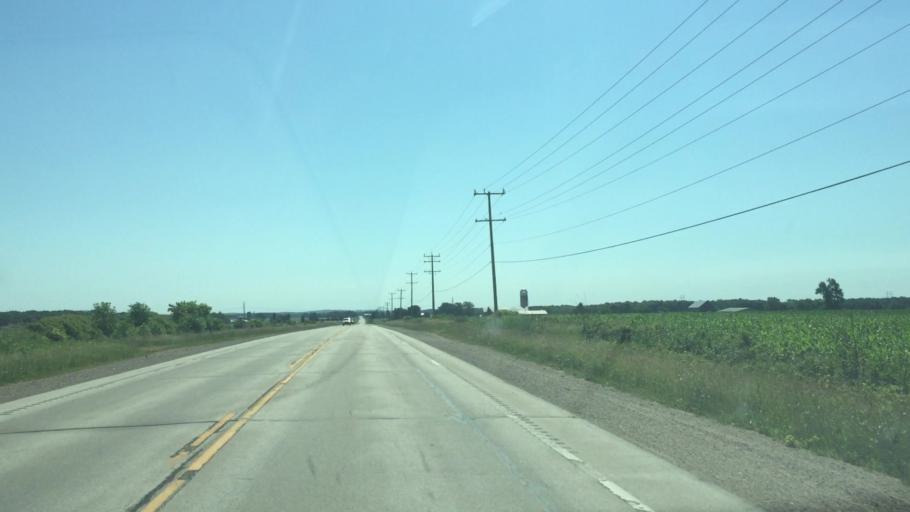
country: US
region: Wisconsin
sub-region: Calumet County
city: Sherwood
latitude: 44.1407
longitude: -88.2336
